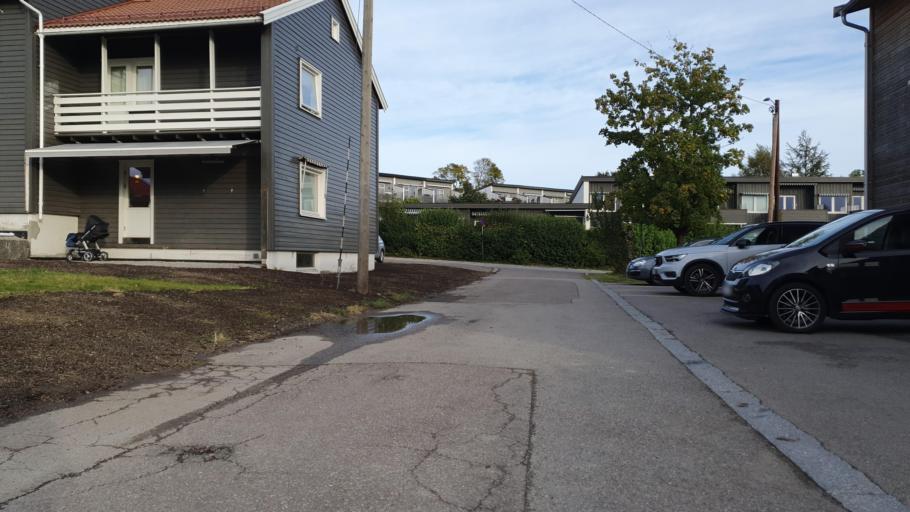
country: NO
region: Vestfold
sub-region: Tonsberg
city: Tonsberg
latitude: 59.2761
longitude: 10.4228
